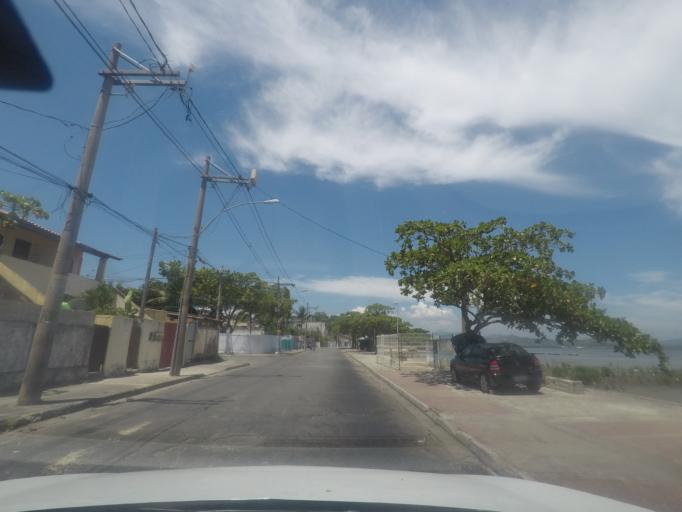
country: BR
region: Rio de Janeiro
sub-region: Itaguai
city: Itaguai
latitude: -22.9852
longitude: -43.6866
